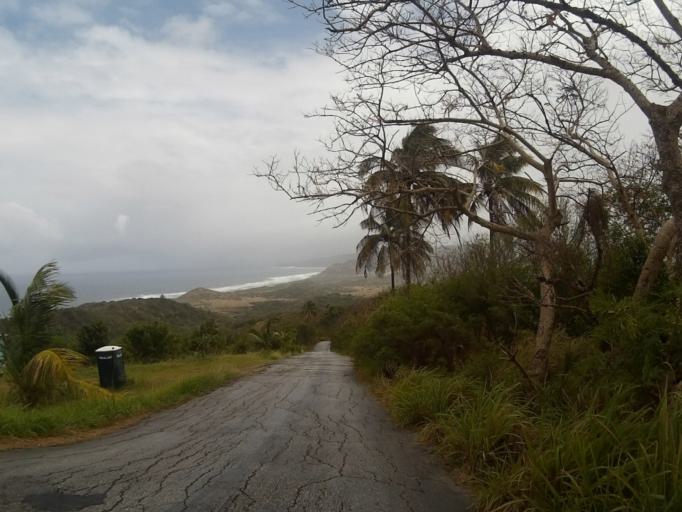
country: BB
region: Saint Andrew
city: Greenland
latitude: 13.2744
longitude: -59.5794
